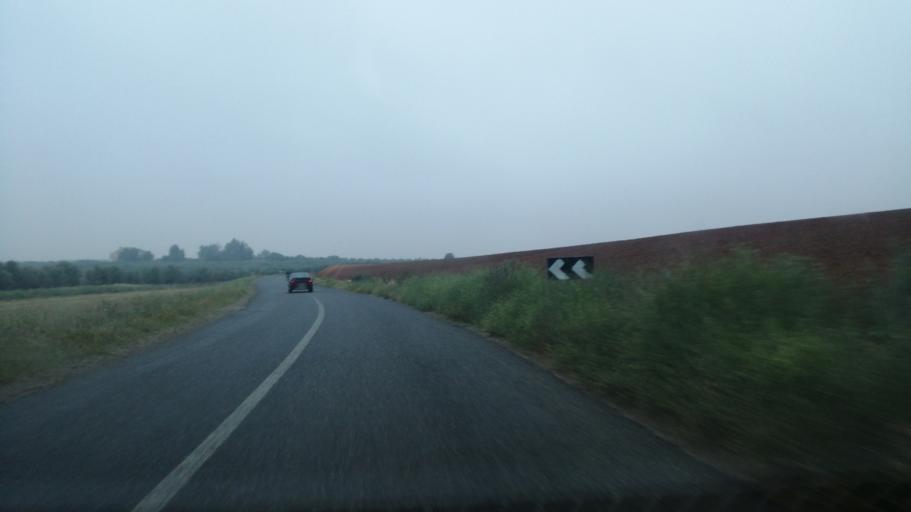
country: MA
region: Rabat-Sale-Zemmour-Zaer
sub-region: Khemisset
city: Tiflet
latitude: 33.7538
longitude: -6.2675
